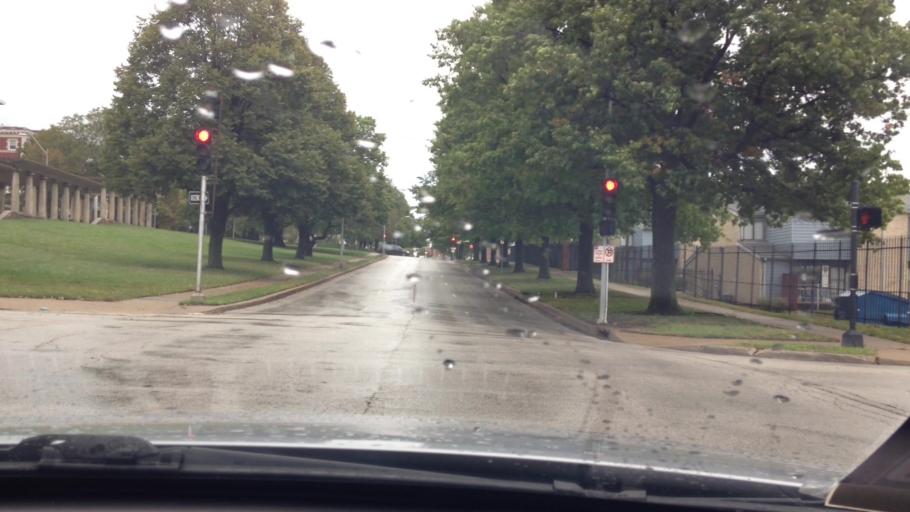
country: US
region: Missouri
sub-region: Jackson County
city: Kansas City
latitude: 39.1004
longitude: -94.5635
